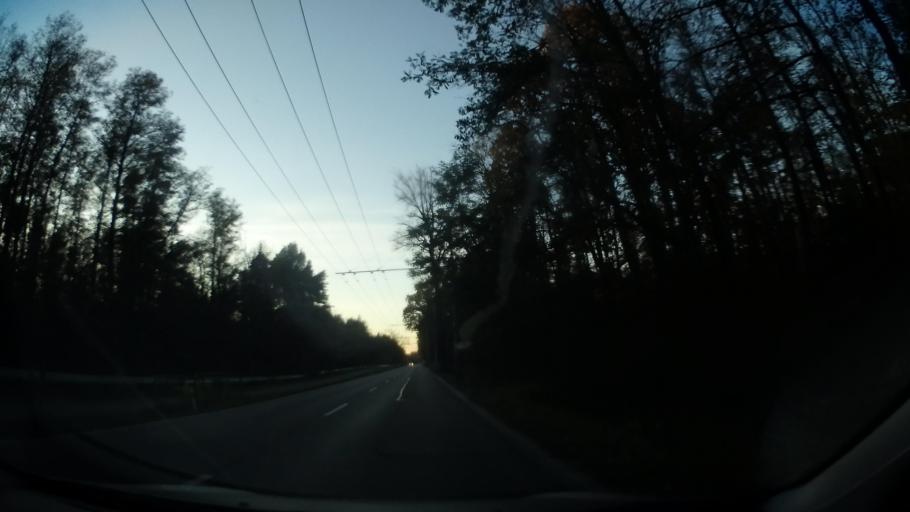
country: CZ
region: Pardubicky
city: Rybitvi
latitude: 50.0687
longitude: 15.6978
